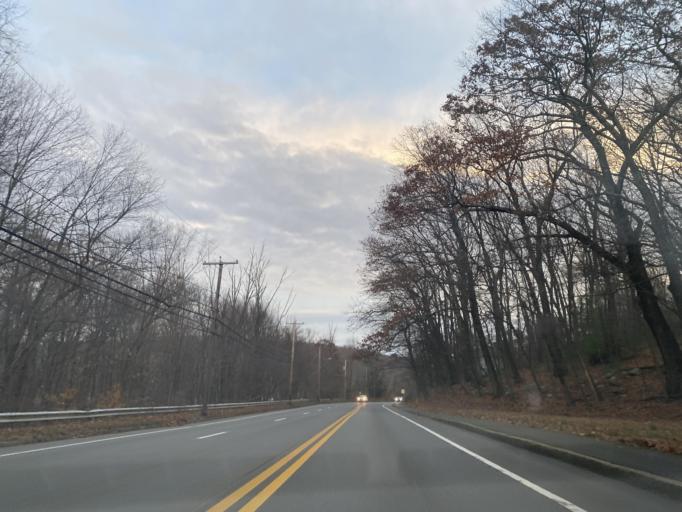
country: US
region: Massachusetts
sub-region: Worcester County
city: Leicester
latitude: 42.2791
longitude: -71.8616
